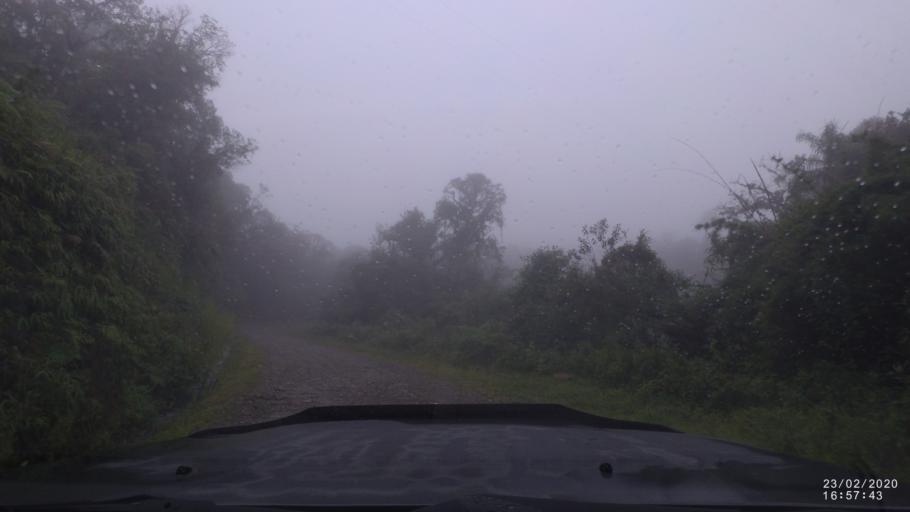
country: BO
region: Cochabamba
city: Colomi
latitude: -17.1040
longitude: -65.9760
